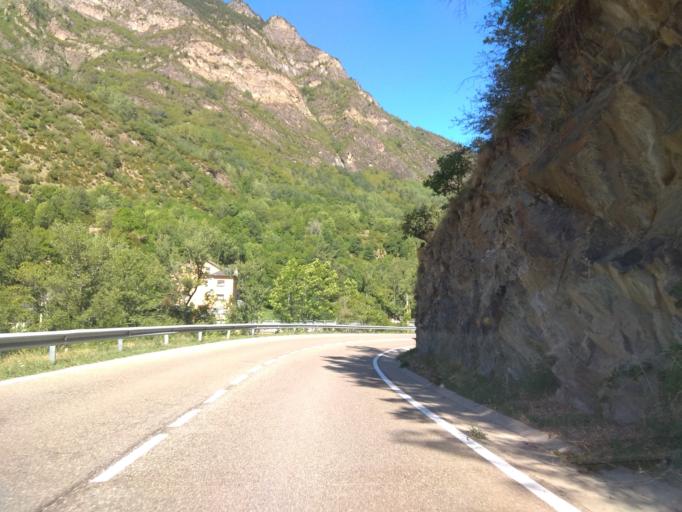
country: ES
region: Catalonia
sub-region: Provincia de Lleida
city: Vielha
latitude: 42.5306
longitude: 0.8333
